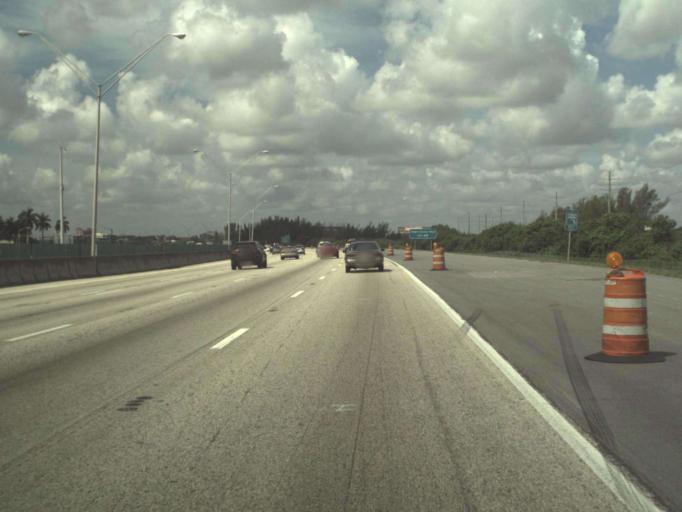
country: US
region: Florida
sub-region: Palm Beach County
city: Boca Raton
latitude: 26.3797
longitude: -80.1127
